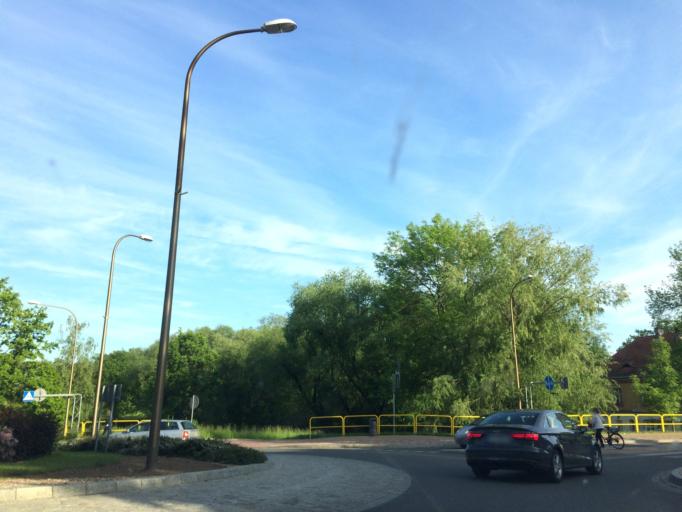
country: PL
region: Lower Silesian Voivodeship
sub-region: Powiat swidnicki
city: Swidnica
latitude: 50.8357
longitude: 16.4852
